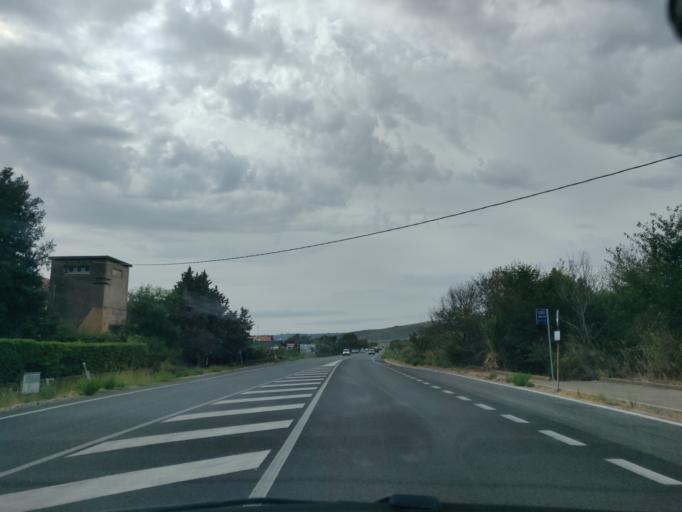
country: IT
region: Latium
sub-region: Citta metropolitana di Roma Capitale
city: Santa Marinella
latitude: 42.0322
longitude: 11.9337
